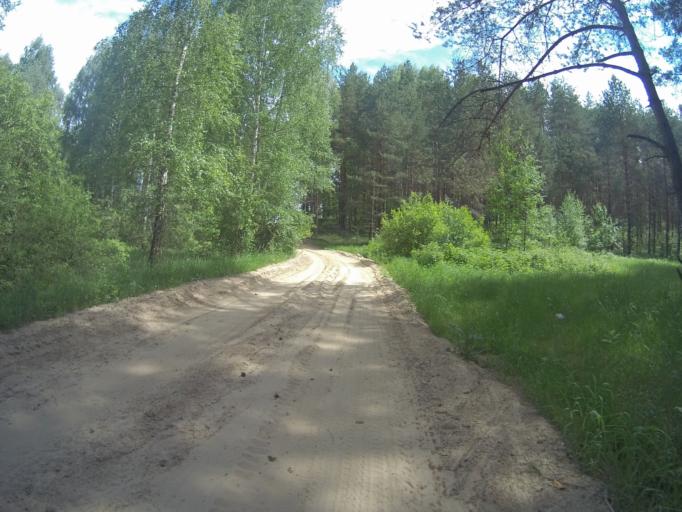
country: RU
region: Vladimir
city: Raduzhnyy
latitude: 56.0225
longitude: 40.2944
